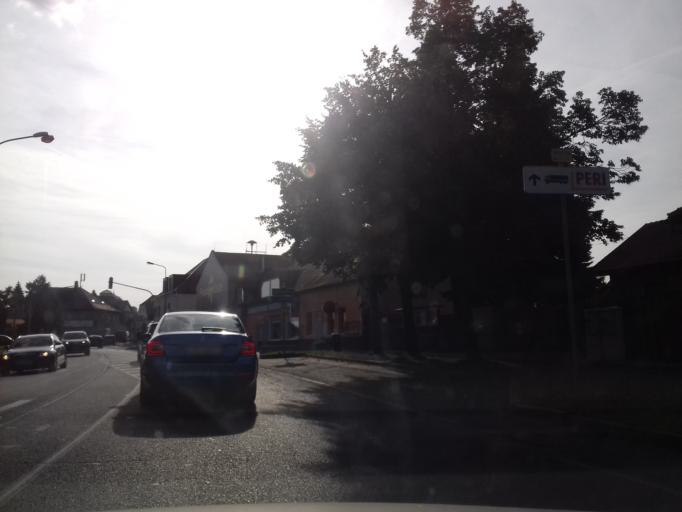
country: CZ
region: Central Bohemia
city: Jesenice
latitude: 49.9679
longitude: 14.5136
